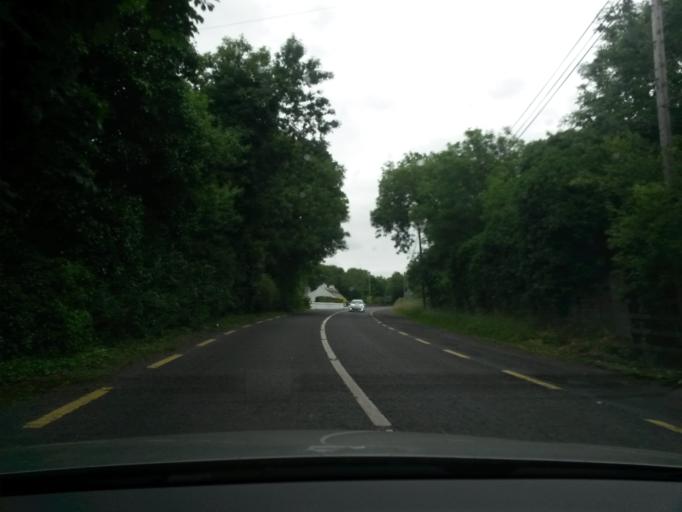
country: IE
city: Ballisodare
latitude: 54.2037
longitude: -8.5663
